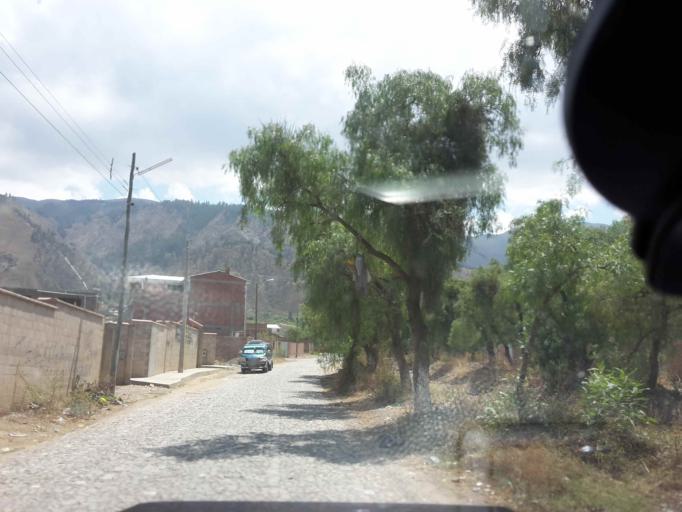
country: BO
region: Cochabamba
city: Cochabamba
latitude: -17.3285
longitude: -66.2240
